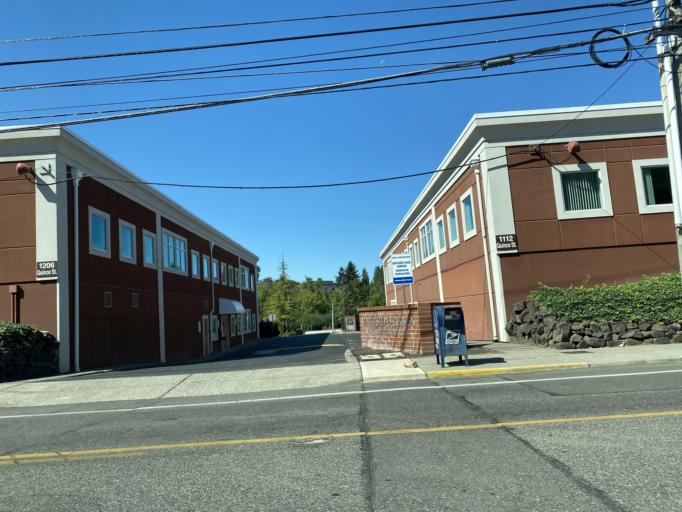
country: US
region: Washington
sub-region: Thurston County
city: Olympia
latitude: 47.0382
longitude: -122.8874
